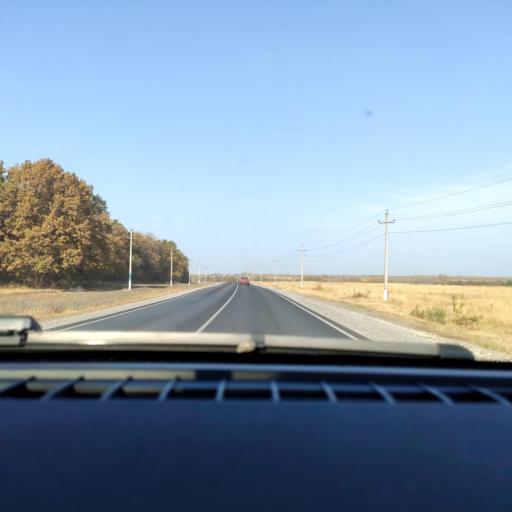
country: RU
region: Voronezj
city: Novaya Usman'
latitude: 51.6884
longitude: 39.3964
